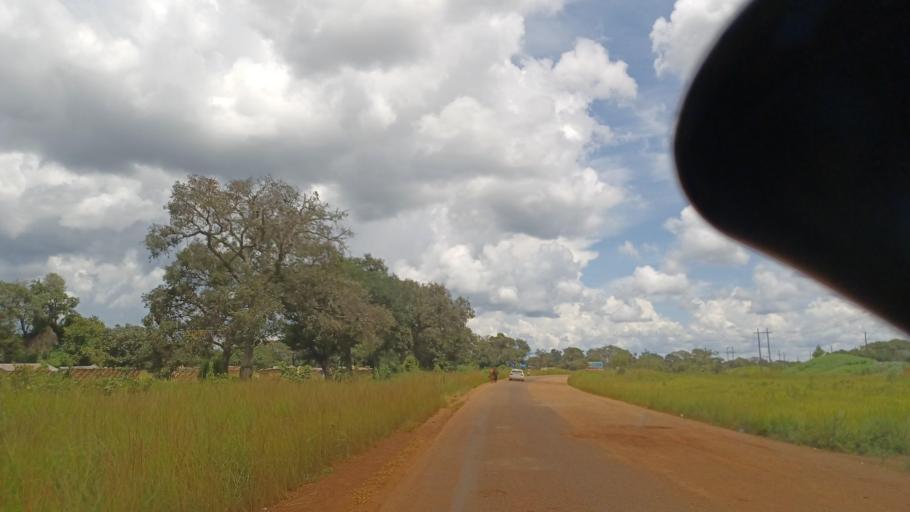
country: ZM
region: North-Western
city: Solwezi
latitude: -12.4807
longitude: 26.1980
